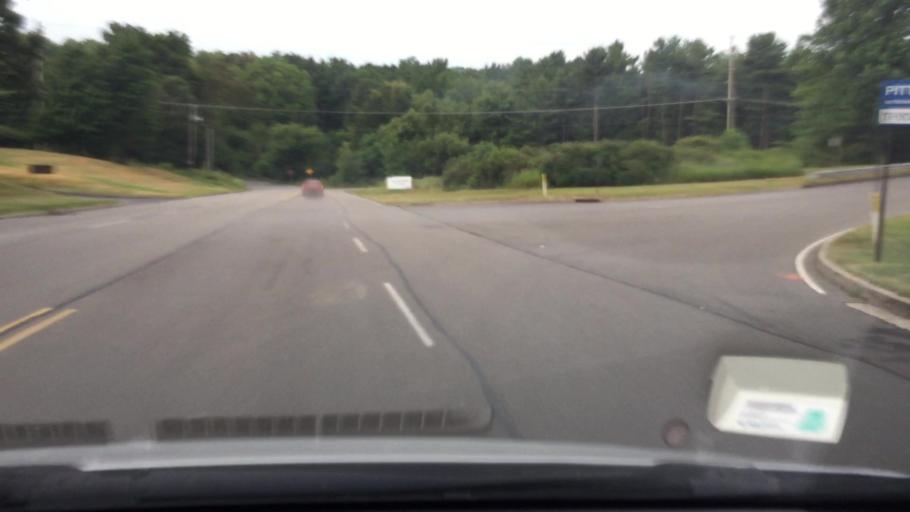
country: US
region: Pennsylvania
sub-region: Butler County
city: Cranberry Township
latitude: 40.6646
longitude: -80.1009
